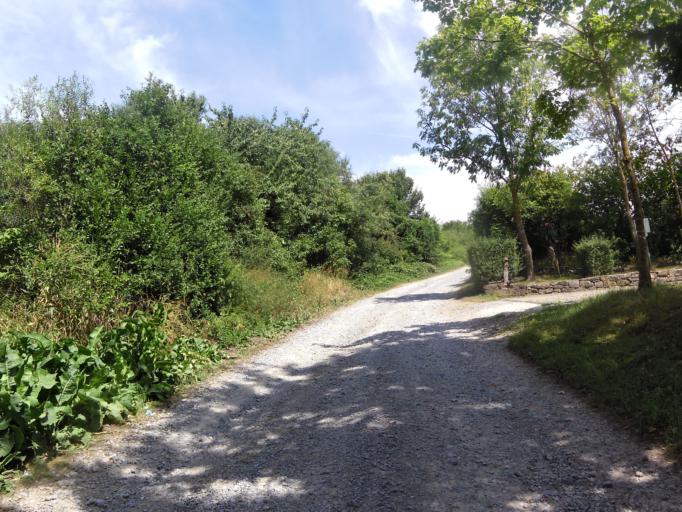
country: DE
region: Bavaria
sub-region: Regierungsbezirk Unterfranken
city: Gerbrunn
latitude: 49.7921
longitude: 10.0047
